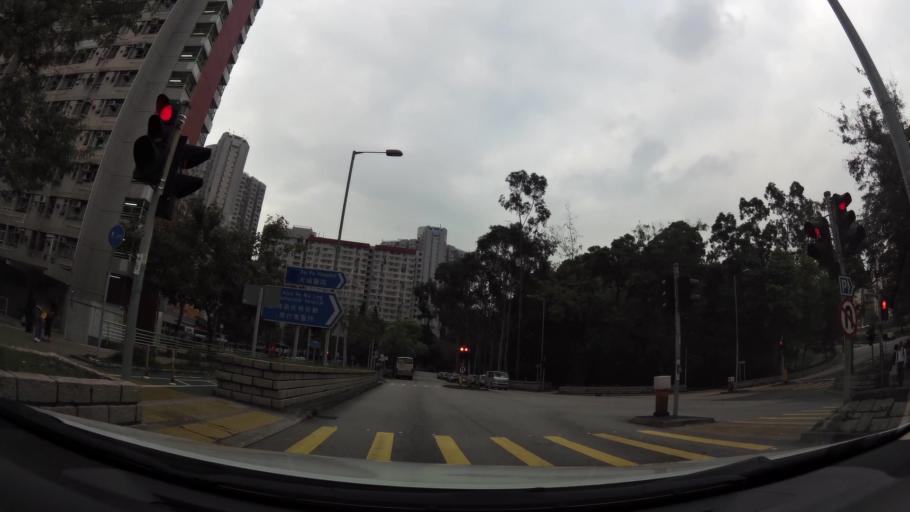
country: HK
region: Tai Po
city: Tai Po
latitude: 22.4573
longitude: 114.1721
